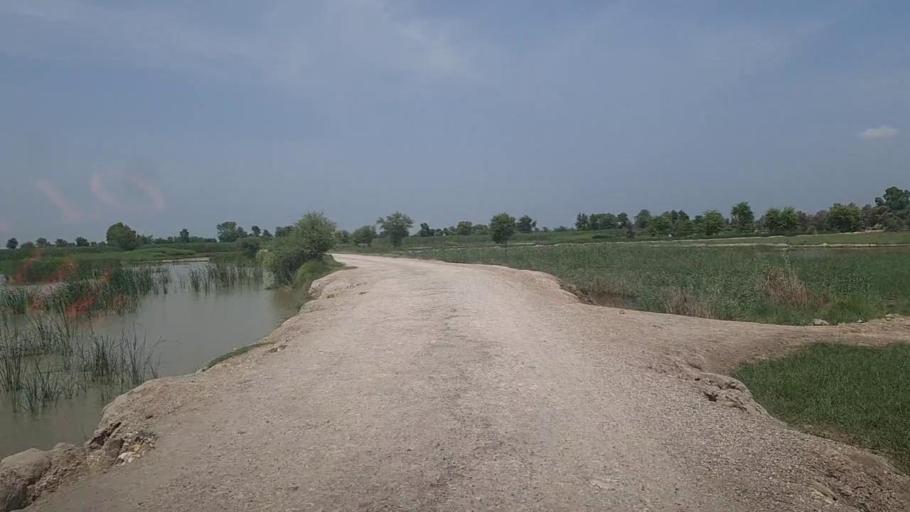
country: PK
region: Sindh
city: Ubauro
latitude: 28.1771
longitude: 69.7683
